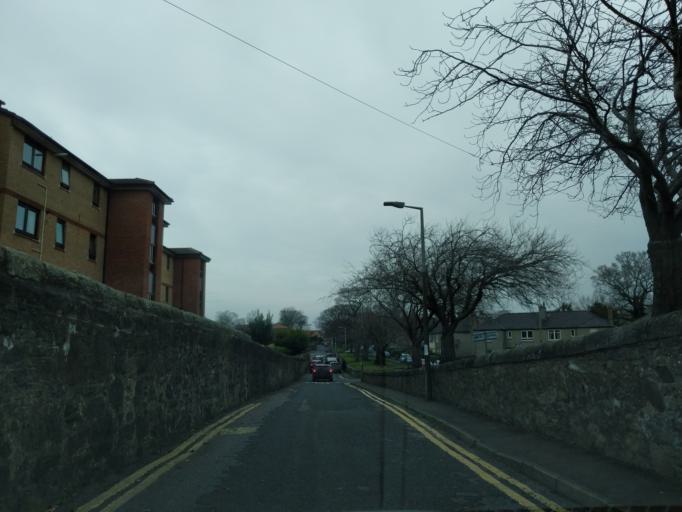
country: GB
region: Scotland
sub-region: Edinburgh
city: Edinburgh
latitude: 55.9703
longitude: -3.1973
